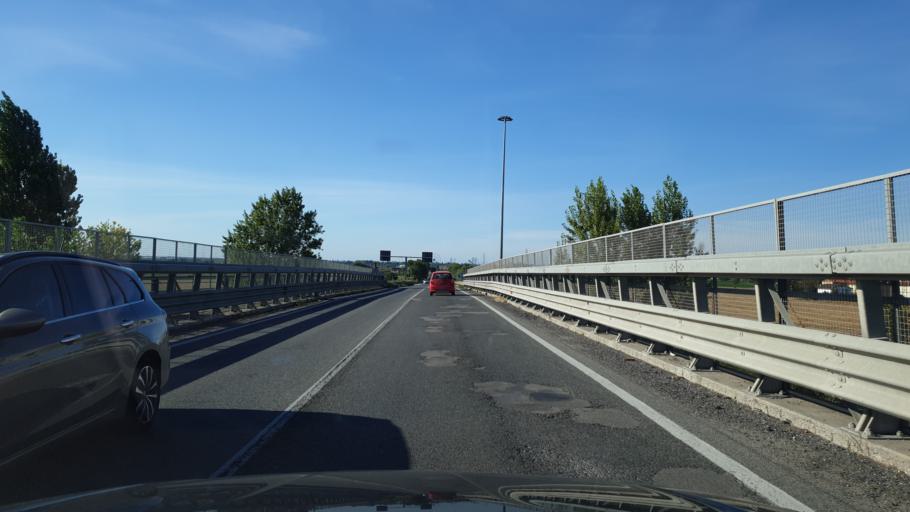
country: IT
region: Emilia-Romagna
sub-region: Provincia di Ravenna
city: Savio
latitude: 44.3037
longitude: 12.2898
